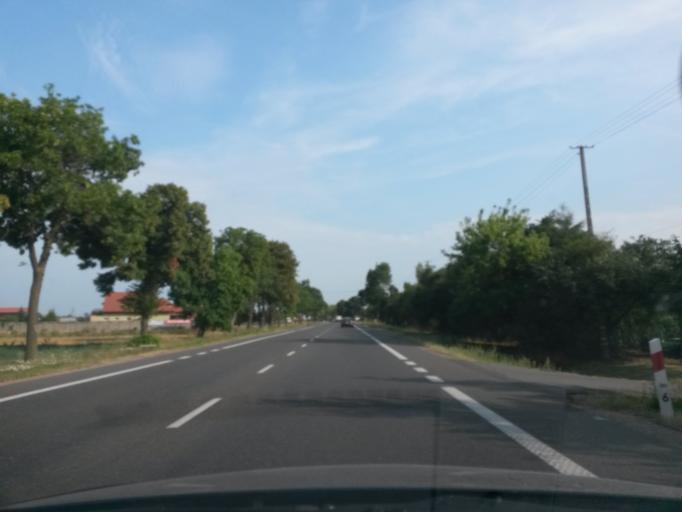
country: PL
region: Masovian Voivodeship
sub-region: Powiat sierpecki
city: Sierpc
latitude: 52.8567
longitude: 19.6829
